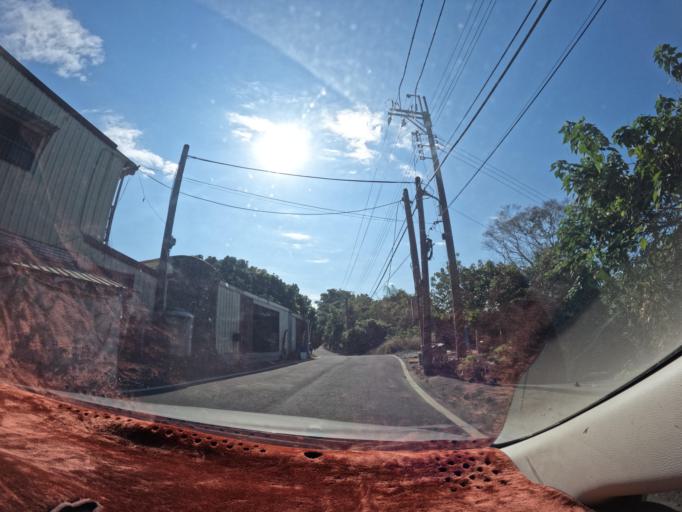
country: TW
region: Taiwan
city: Yujing
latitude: 23.0263
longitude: 120.3846
